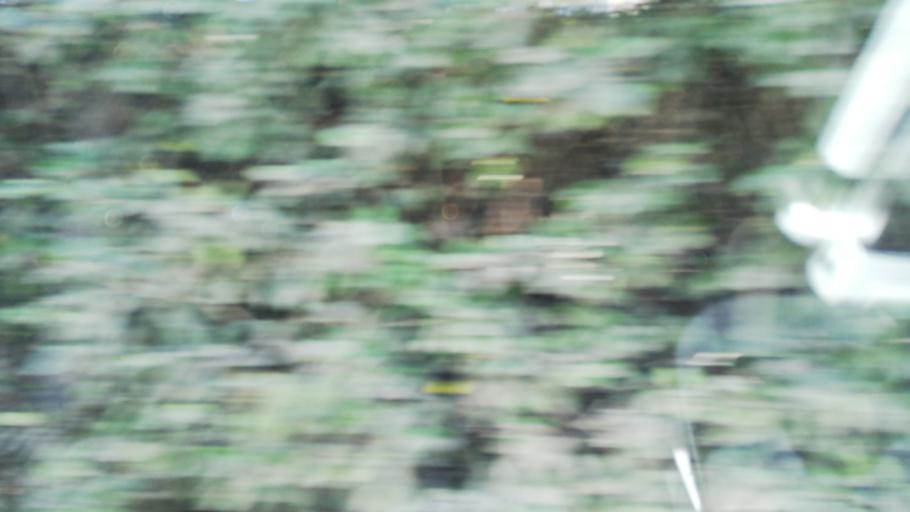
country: MU
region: Plaines Wilhems
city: Ebene
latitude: -20.2294
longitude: 57.4692
